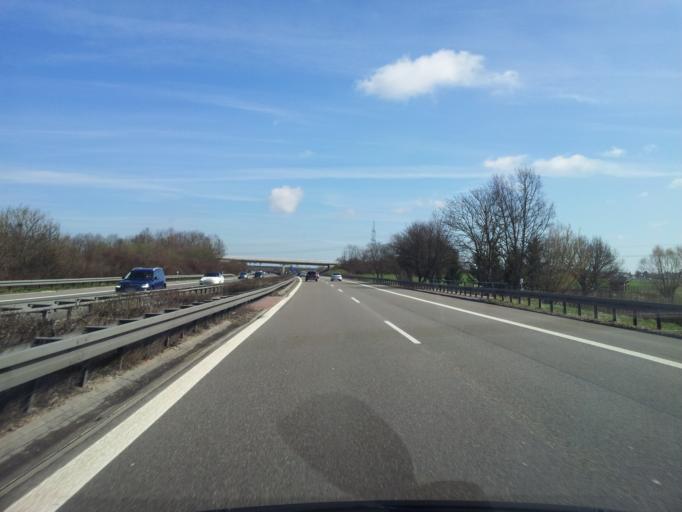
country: DE
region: Baden-Wuerttemberg
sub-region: Regierungsbezirk Stuttgart
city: Bondorf
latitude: 48.4887
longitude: 8.8250
